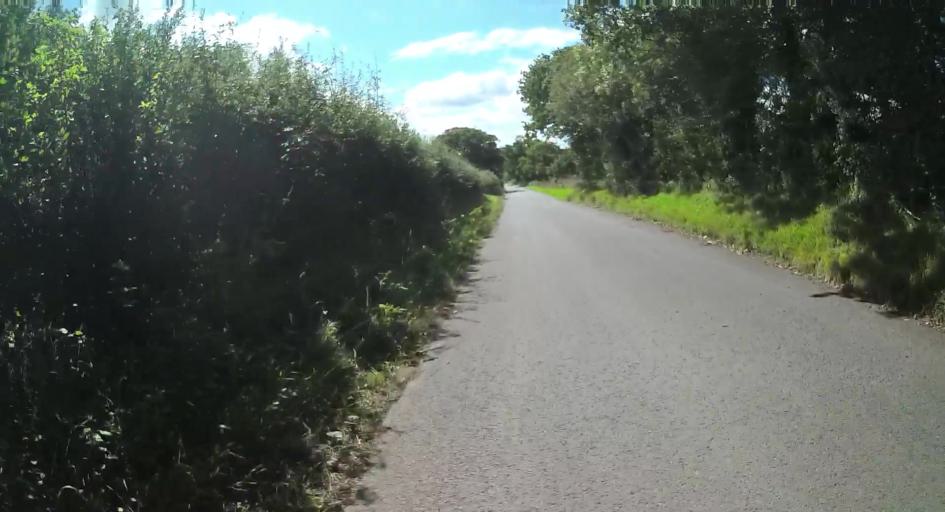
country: GB
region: England
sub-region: Isle of Wight
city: East Cowes
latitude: 50.7304
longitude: -1.2598
